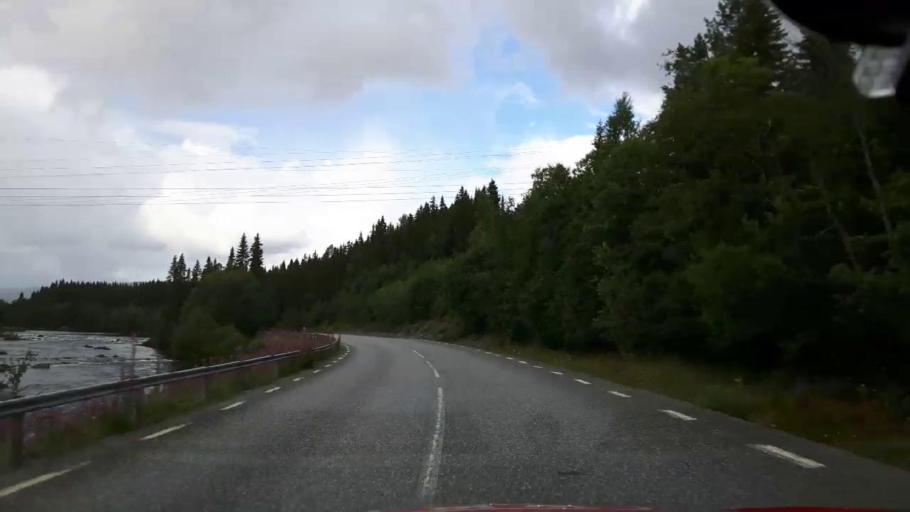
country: SE
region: Vaesterbotten
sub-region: Vilhelmina Kommun
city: Sjoberg
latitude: 64.9432
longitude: 15.8289
